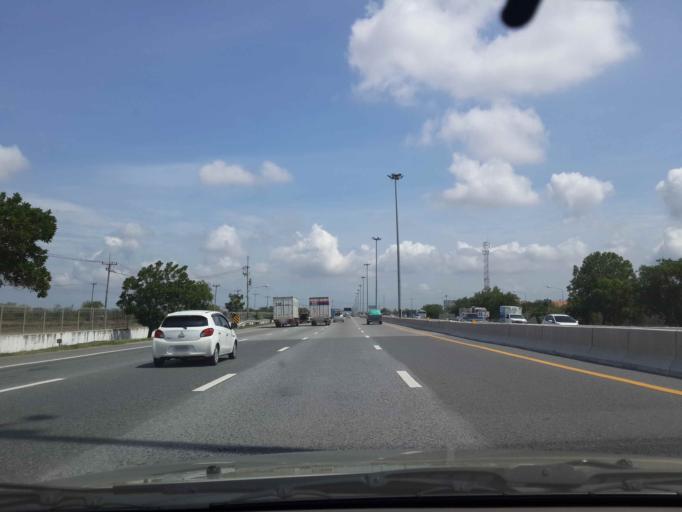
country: TH
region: Chachoengsao
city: Bang Pakong
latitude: 13.5216
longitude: 101.0237
